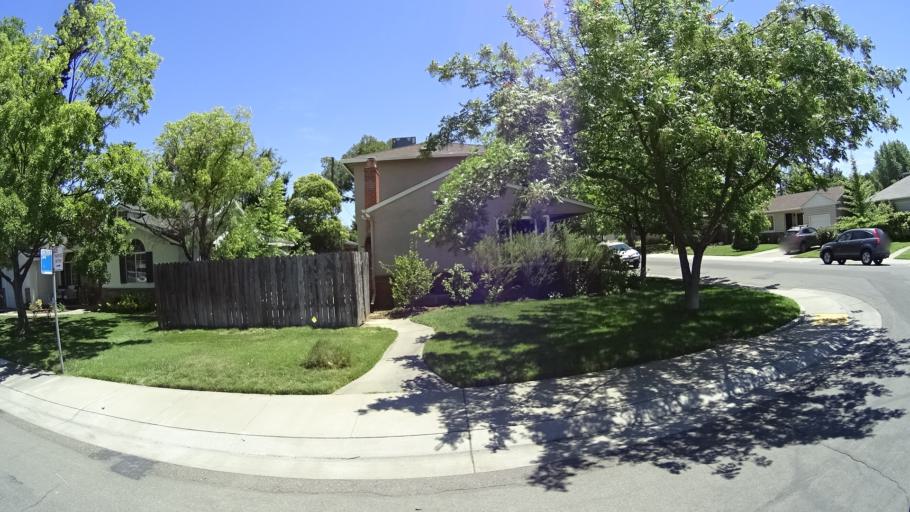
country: US
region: California
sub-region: Sacramento County
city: Sacramento
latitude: 38.5765
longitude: -121.4428
